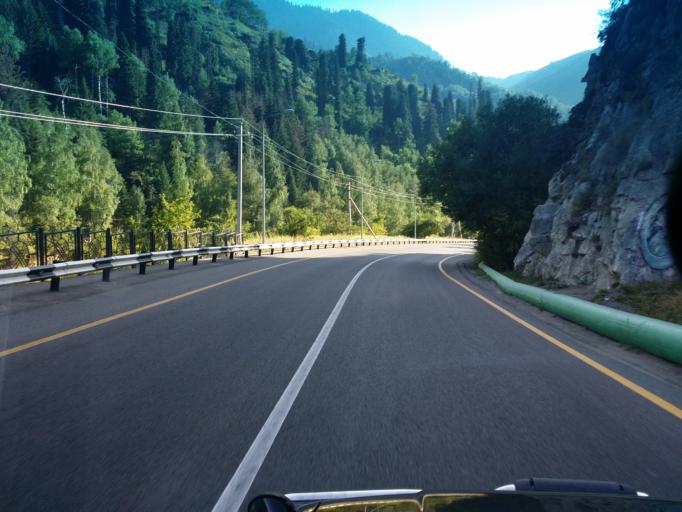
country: KZ
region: Almaty Qalasy
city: Almaty
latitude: 43.1624
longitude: 77.0457
